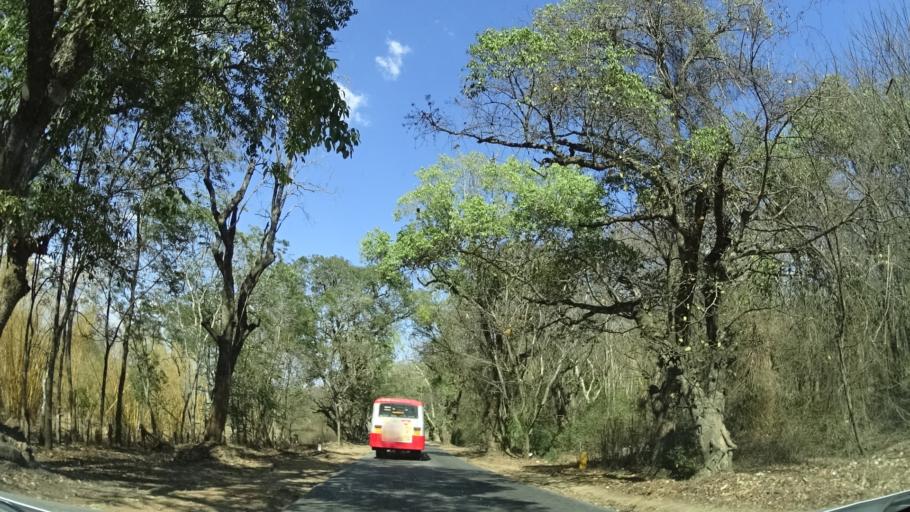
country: IN
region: Karnataka
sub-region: Chikmagalur
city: Chikmagalur
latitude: 13.2769
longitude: 75.7296
